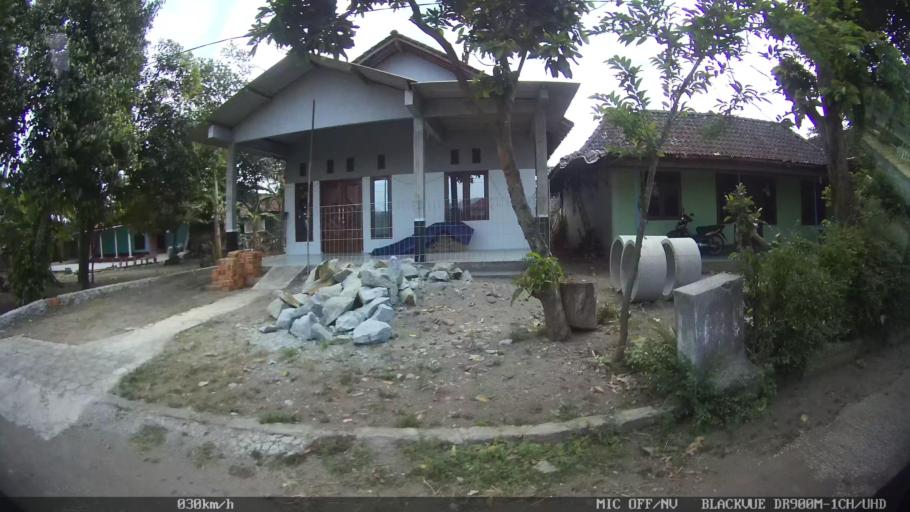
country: ID
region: Central Java
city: Candi Prambanan
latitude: -7.8155
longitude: 110.4787
